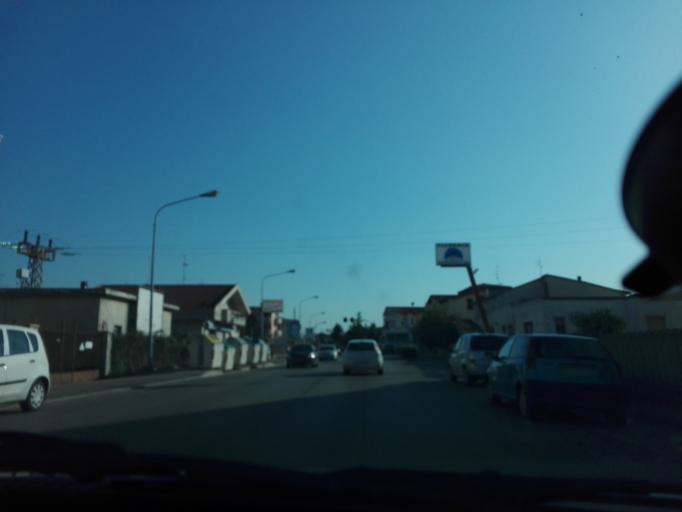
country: IT
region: Abruzzo
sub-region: Provincia di Pescara
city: Montesilvano Marina
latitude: 42.4948
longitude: 14.1263
